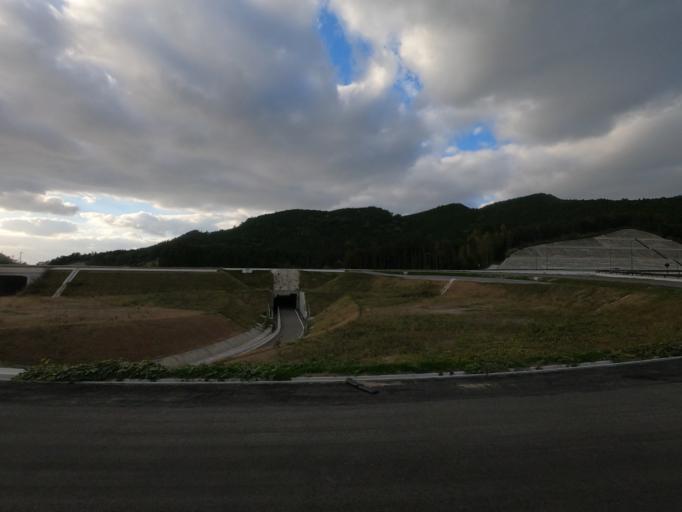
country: JP
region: Kumamoto
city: Minamata
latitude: 32.2110
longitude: 130.4261
